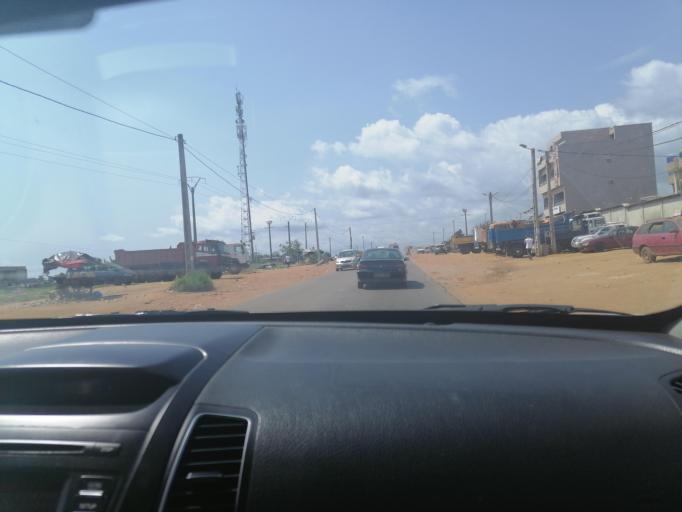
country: CI
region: Lagunes
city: Songon
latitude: 5.3385
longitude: -4.1407
